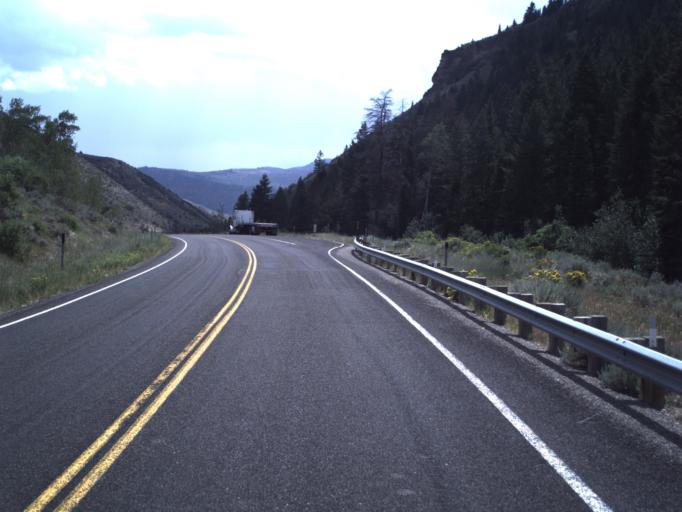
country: US
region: Utah
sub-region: Summit County
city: Francis
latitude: 40.4723
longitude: -110.9086
